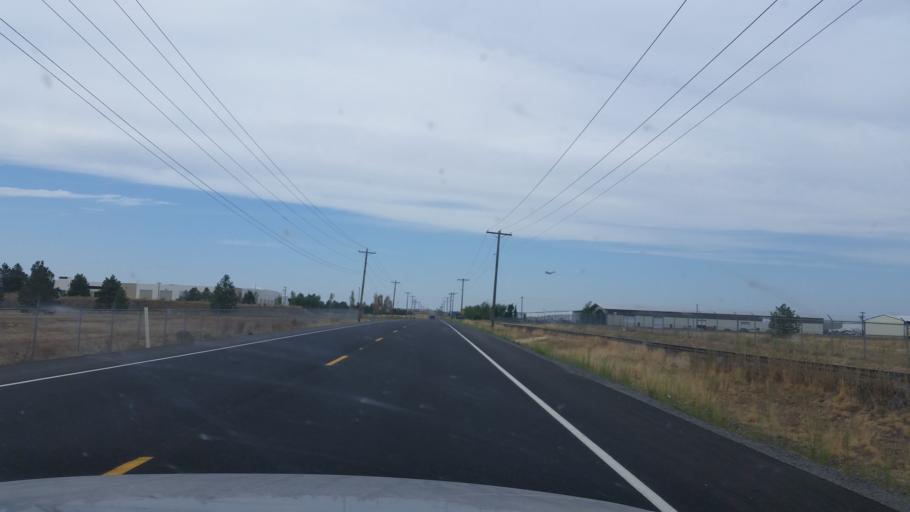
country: US
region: Washington
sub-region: Spokane County
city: Airway Heights
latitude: 47.6283
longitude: -117.5841
